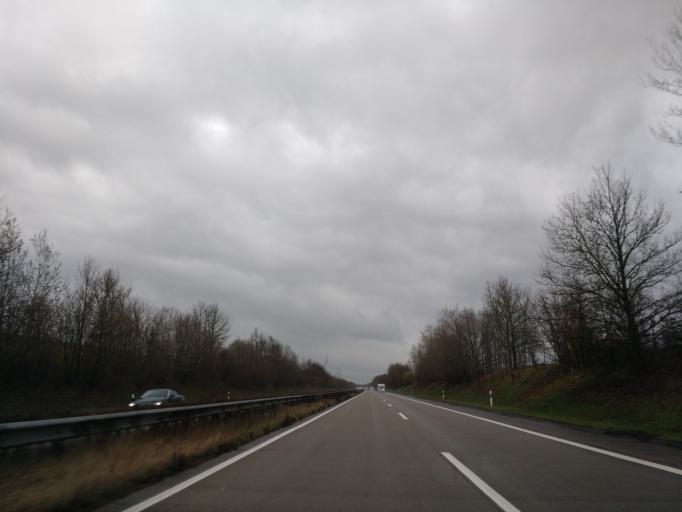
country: DE
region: Lower Saxony
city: Midlum
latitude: 53.6577
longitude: 8.6597
